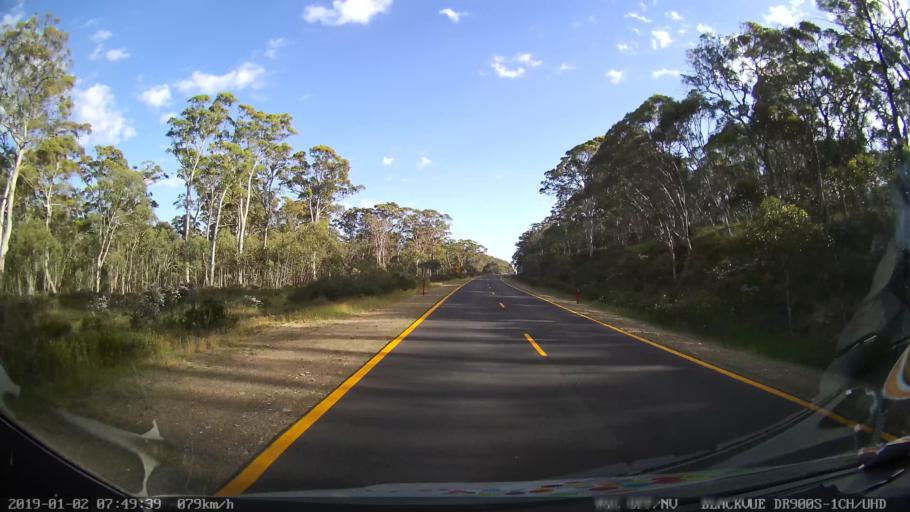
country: AU
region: New South Wales
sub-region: Tumut Shire
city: Tumut
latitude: -35.7392
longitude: 148.5229
